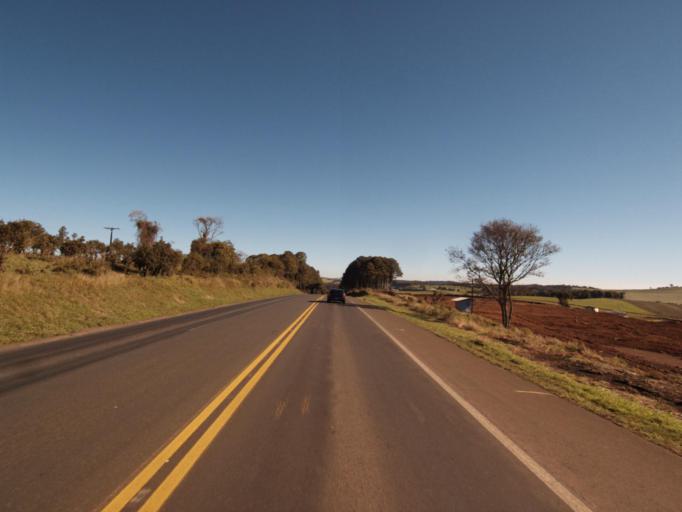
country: BR
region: Santa Catarina
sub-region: Xanxere
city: Xanxere
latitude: -26.9067
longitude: -52.4661
